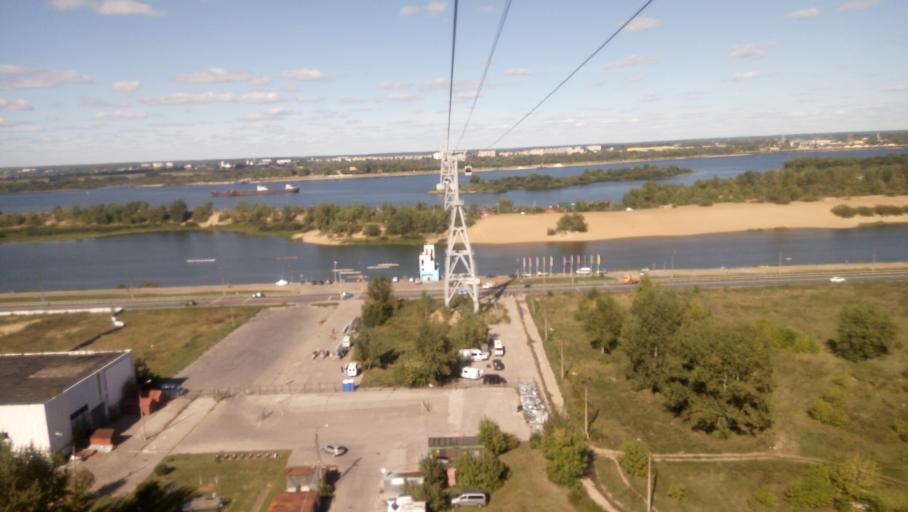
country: RU
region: Nizjnij Novgorod
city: Nizhniy Novgorod
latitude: 56.3252
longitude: 44.0402
